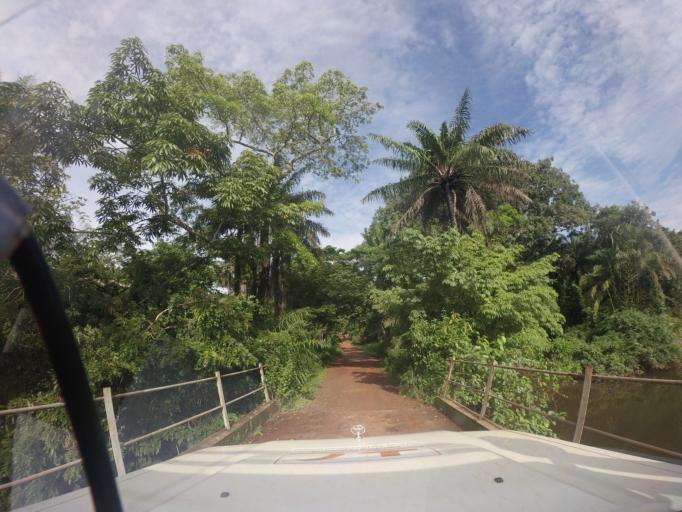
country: SL
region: Northern Province
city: Kambia
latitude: 9.1162
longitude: -12.9467
